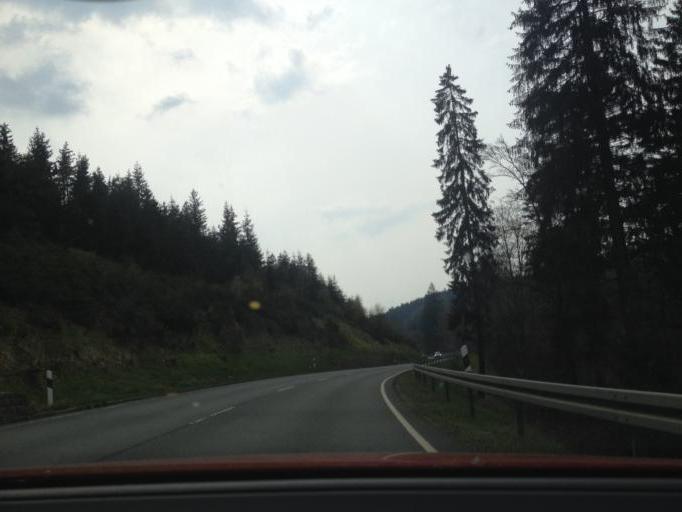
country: DE
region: Bavaria
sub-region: Upper Franconia
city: Bischofsgrun
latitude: 50.0496
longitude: 11.7602
